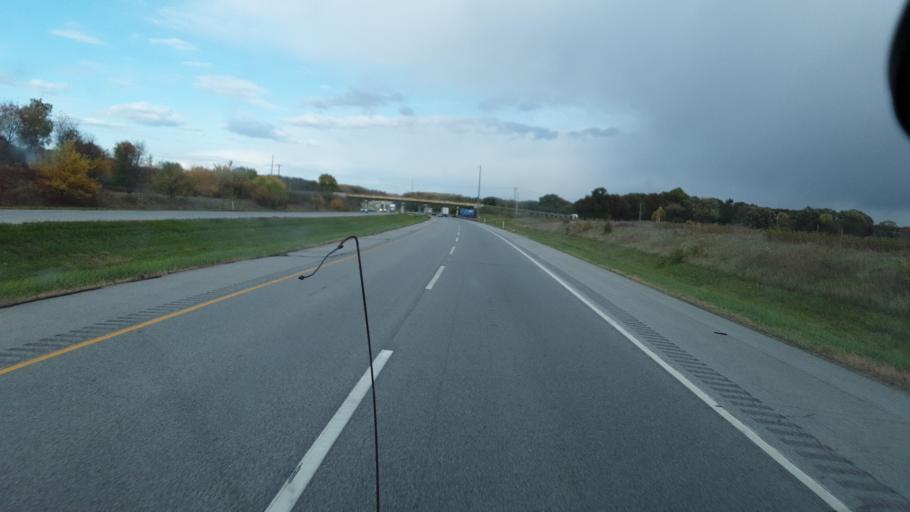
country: US
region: Indiana
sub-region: LaPorte County
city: LaPorte
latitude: 41.6399
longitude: -86.7816
